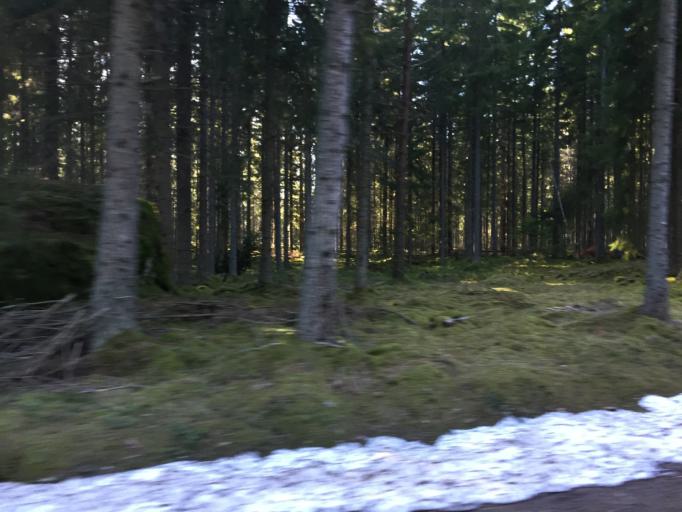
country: SE
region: Soedermanland
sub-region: Vingakers Kommun
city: Vingaker
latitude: 58.9854
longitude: 15.6771
